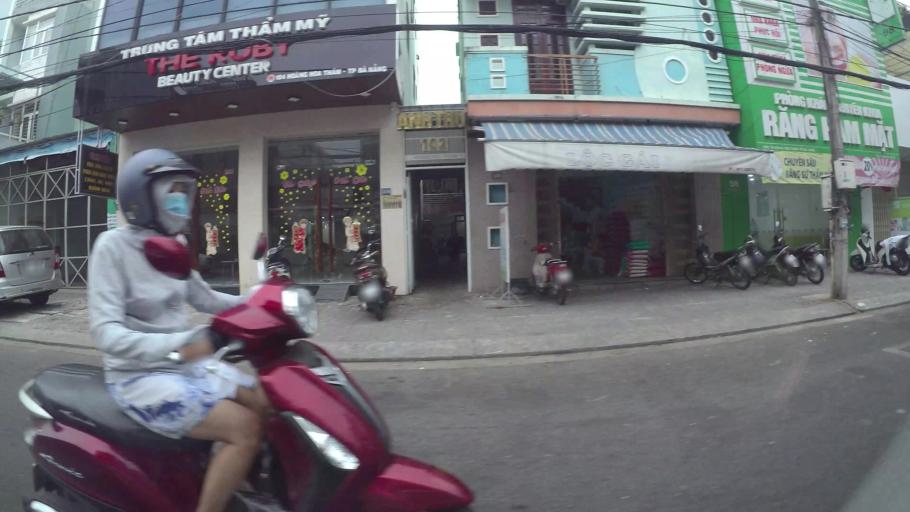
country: VN
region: Da Nang
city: Da Nang
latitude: 16.0675
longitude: 108.2101
